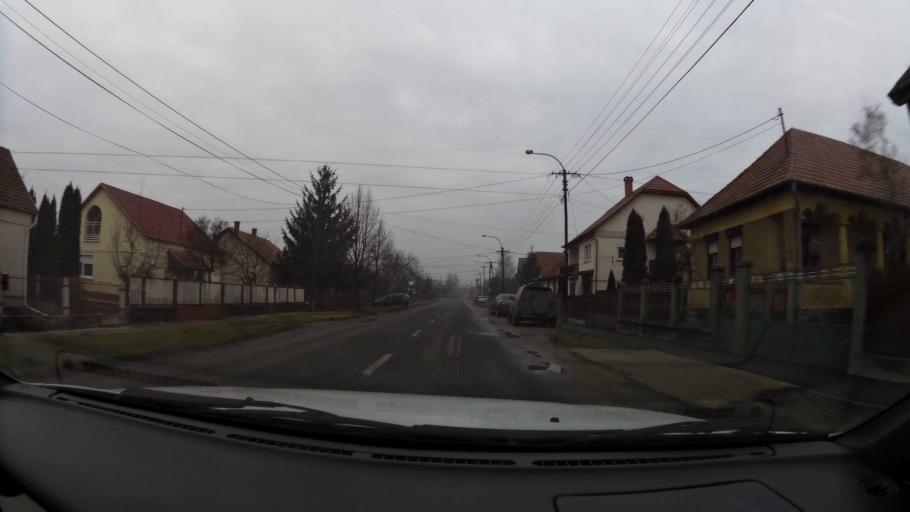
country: HU
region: Borsod-Abauj-Zemplen
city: Izsofalva
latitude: 48.3002
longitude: 20.6565
